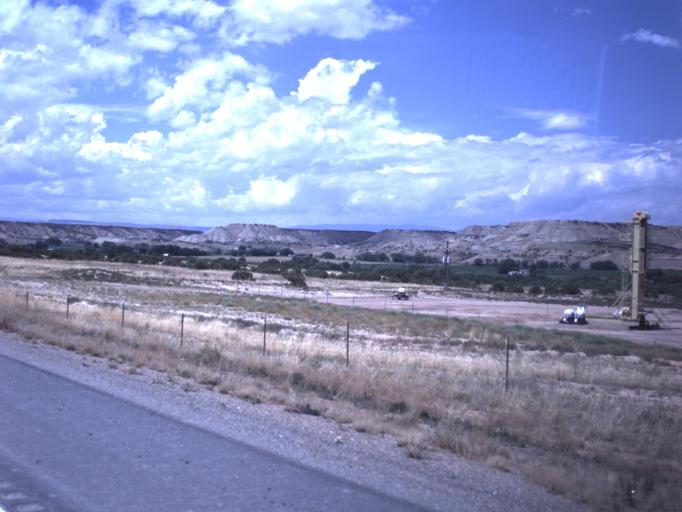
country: US
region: Utah
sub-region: Duchesne County
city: Duchesne
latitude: 40.1718
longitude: -110.3339
